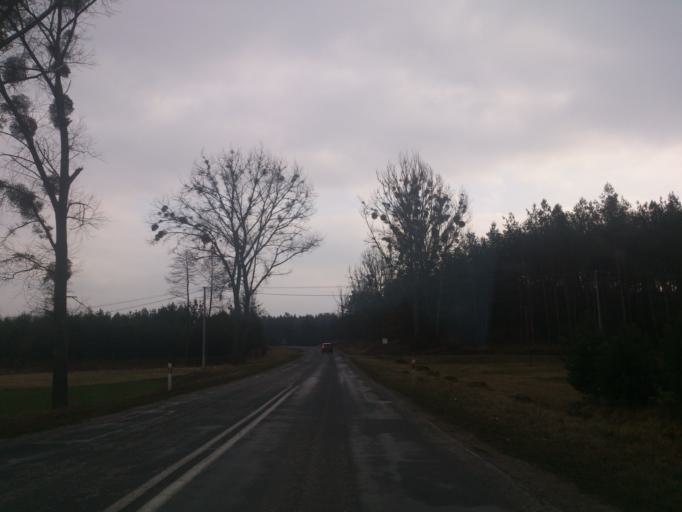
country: PL
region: Kujawsko-Pomorskie
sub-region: Powiat golubsko-dobrzynski
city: Golub-Dobrzyn
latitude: 53.0918
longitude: 19.0491
